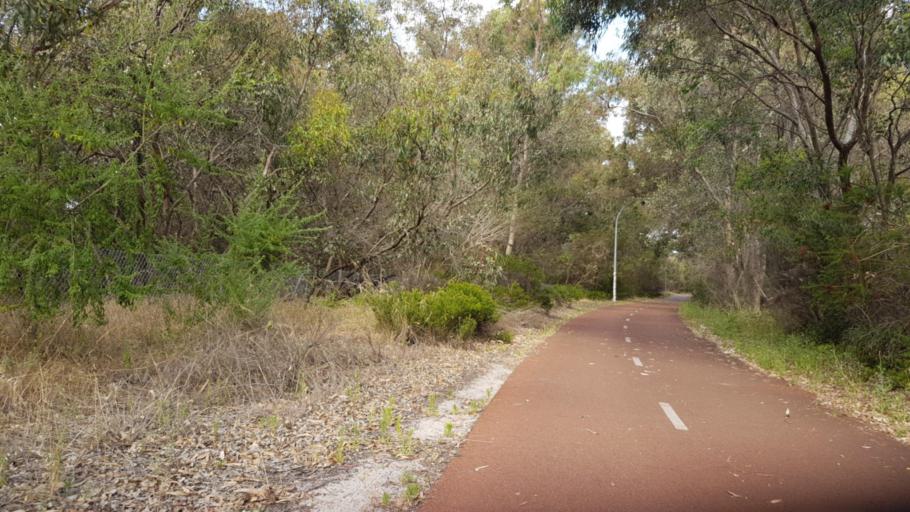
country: AU
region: Western Australia
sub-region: Canning
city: Canning Vale
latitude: -32.0544
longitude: 115.9103
